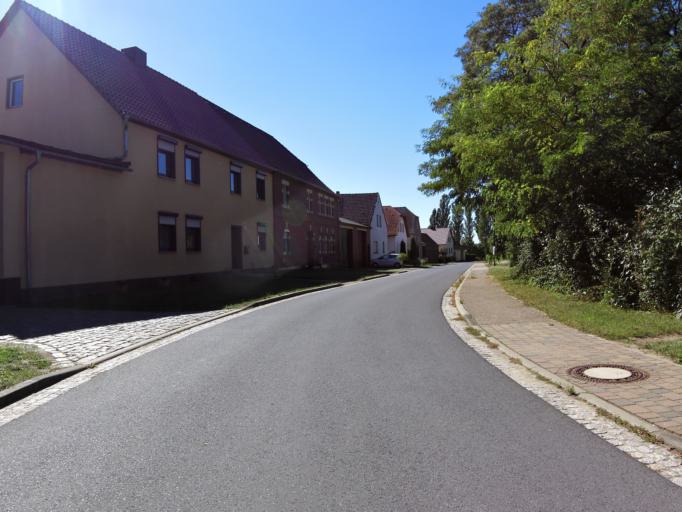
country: DE
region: Saxony-Anhalt
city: Muhlanger
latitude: 51.8516
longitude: 12.7246
